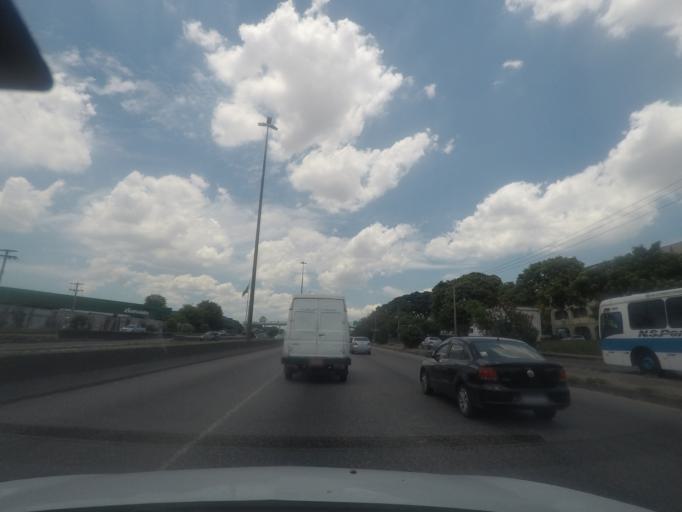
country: BR
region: Rio de Janeiro
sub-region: Sao Joao De Meriti
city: Sao Joao de Meriti
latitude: -22.8258
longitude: -43.3371
